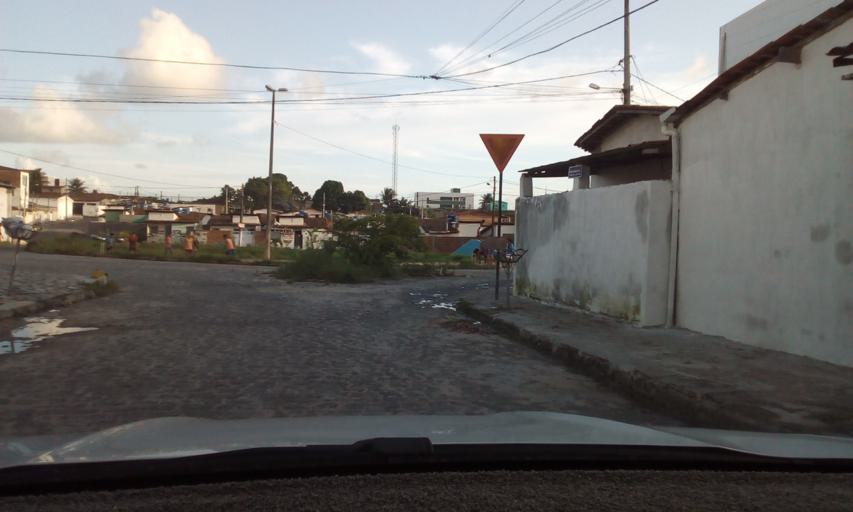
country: BR
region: Paraiba
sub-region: Joao Pessoa
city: Joao Pessoa
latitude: -7.1726
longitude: -34.8829
